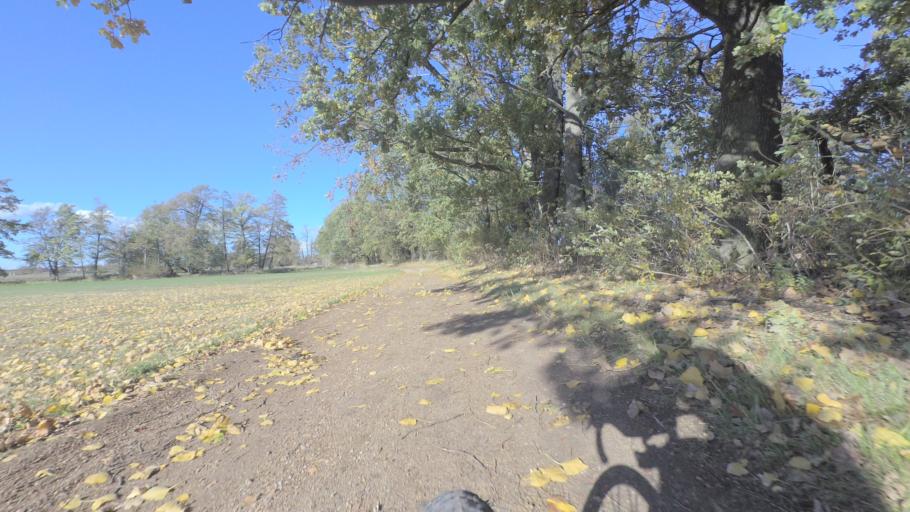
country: DE
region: Saxony
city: Nauwalde
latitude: 51.4380
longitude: 13.3758
